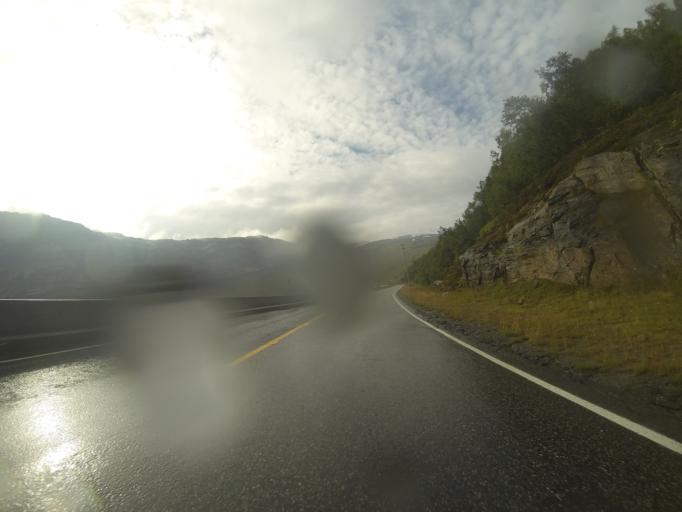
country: NO
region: Hordaland
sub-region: Odda
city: Odda
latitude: 59.8204
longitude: 6.7489
